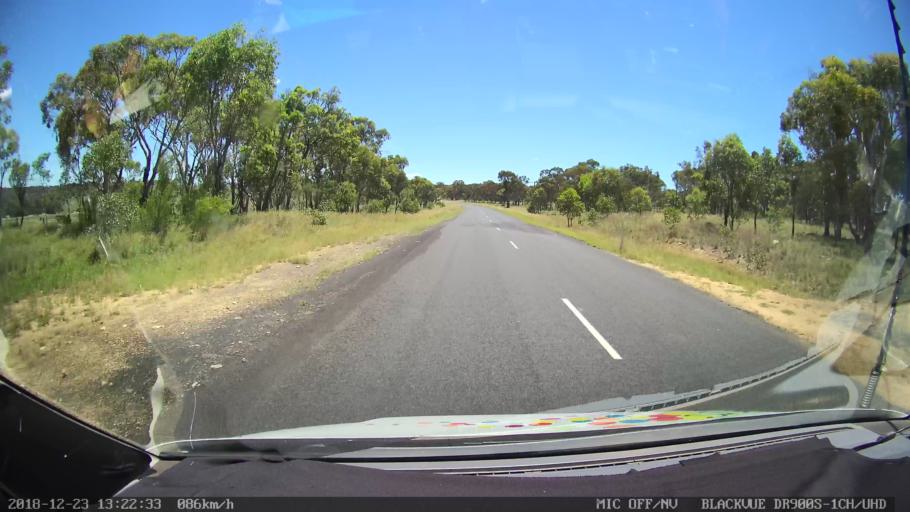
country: AU
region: New South Wales
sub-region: Armidale Dumaresq
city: Armidale
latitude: -30.4798
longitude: 151.4198
